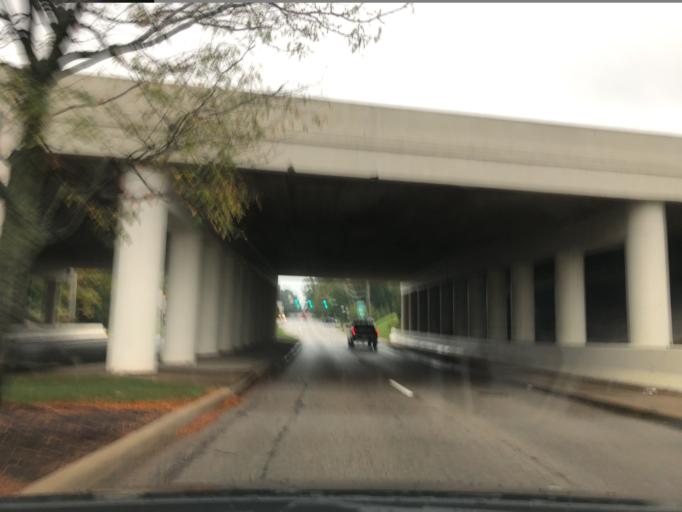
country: US
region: Ohio
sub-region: Hamilton County
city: Blue Ash
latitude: 39.2260
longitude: -84.3777
